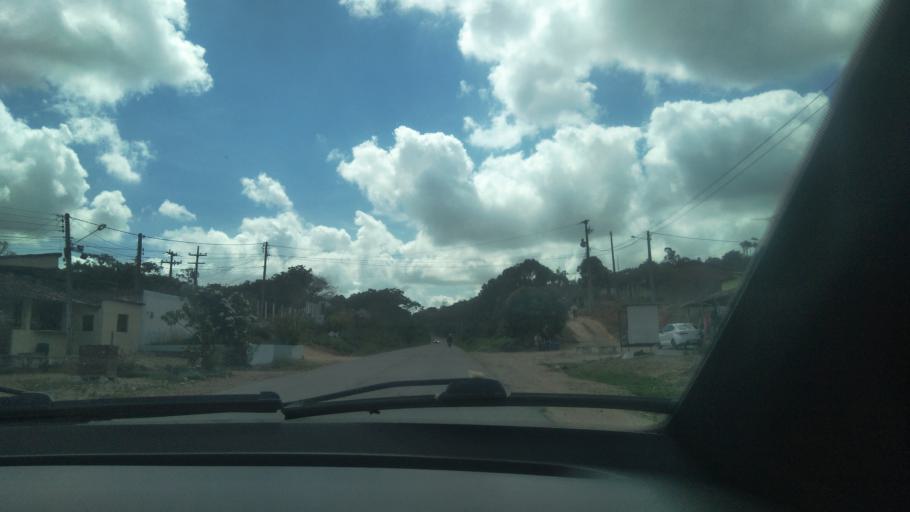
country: BR
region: Pernambuco
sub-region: Vitoria De Santo Antao
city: Vitoria de Santo Antao
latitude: -8.1410
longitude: -35.2707
